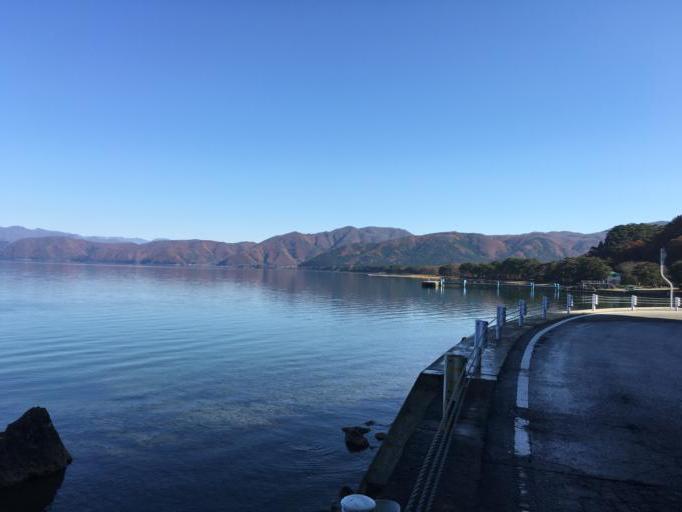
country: JP
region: Fukushima
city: Inawashiro
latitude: 37.4132
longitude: 140.1146
